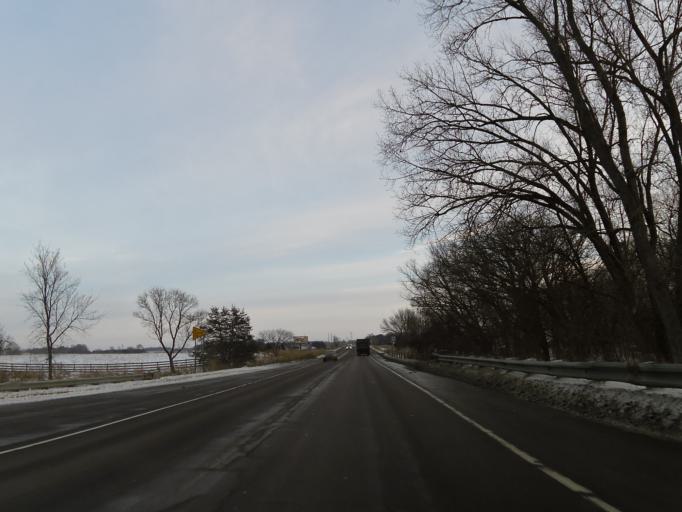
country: US
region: Minnesota
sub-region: Carver County
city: Chaska
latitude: 44.7742
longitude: -93.5891
